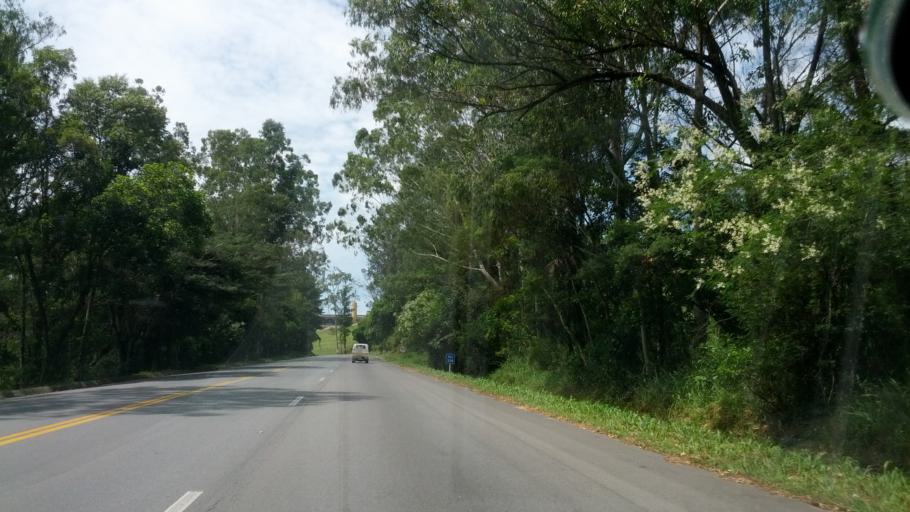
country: BR
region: Santa Catarina
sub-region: Ibirama
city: Ibirama
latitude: -27.1019
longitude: -49.5260
